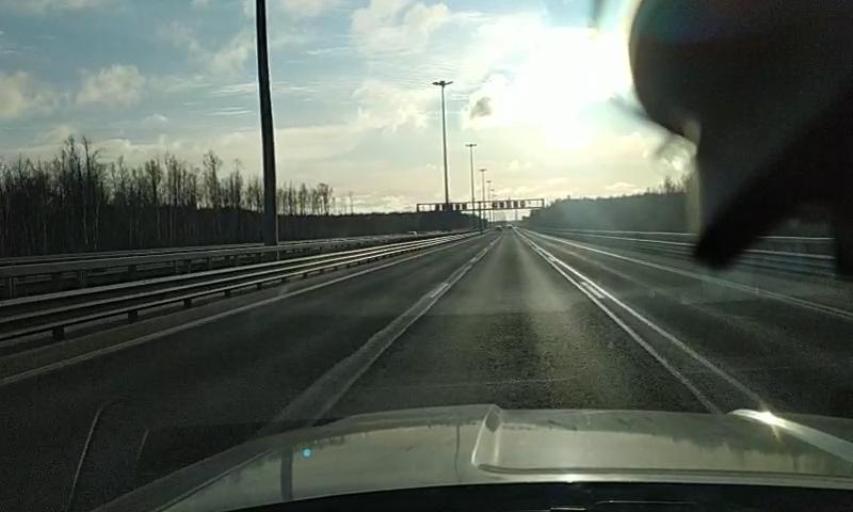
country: RU
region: St.-Petersburg
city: Pesochnyy
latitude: 60.1043
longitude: 30.0876
